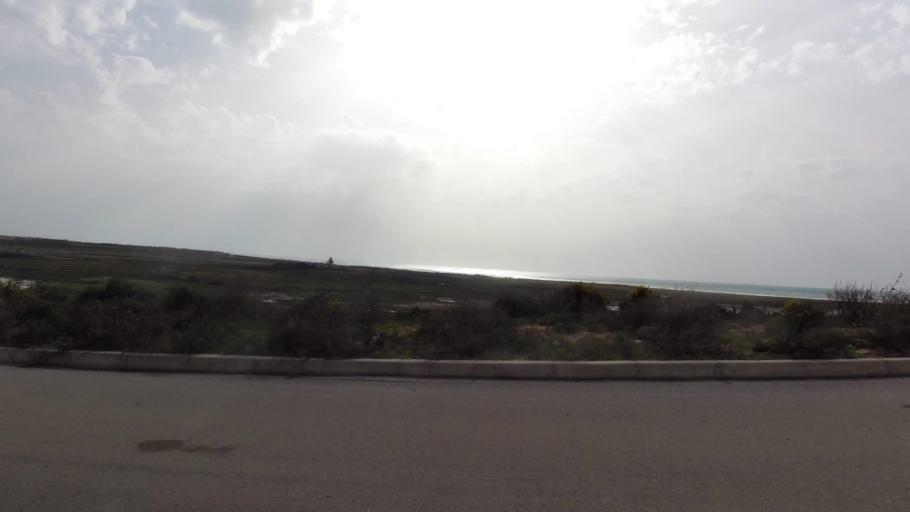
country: MA
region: Tanger-Tetouan
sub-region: Tanger-Assilah
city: Boukhalef
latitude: 35.6983
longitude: -5.9416
